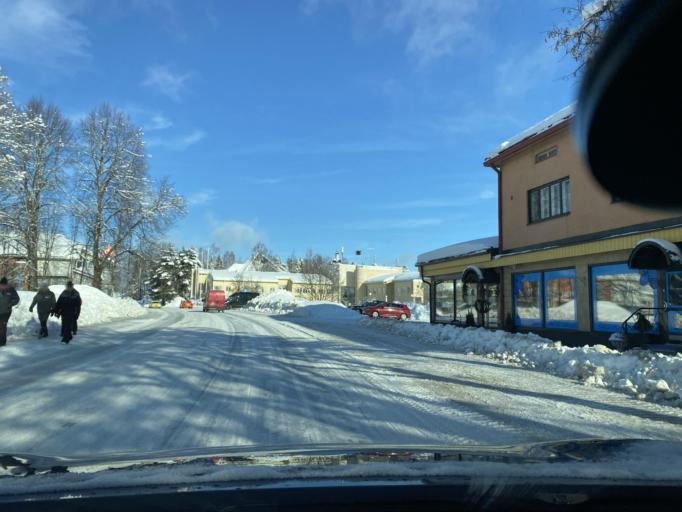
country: FI
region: Southern Savonia
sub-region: Mikkeli
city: Kangasniemi
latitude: 61.9887
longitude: 26.6432
